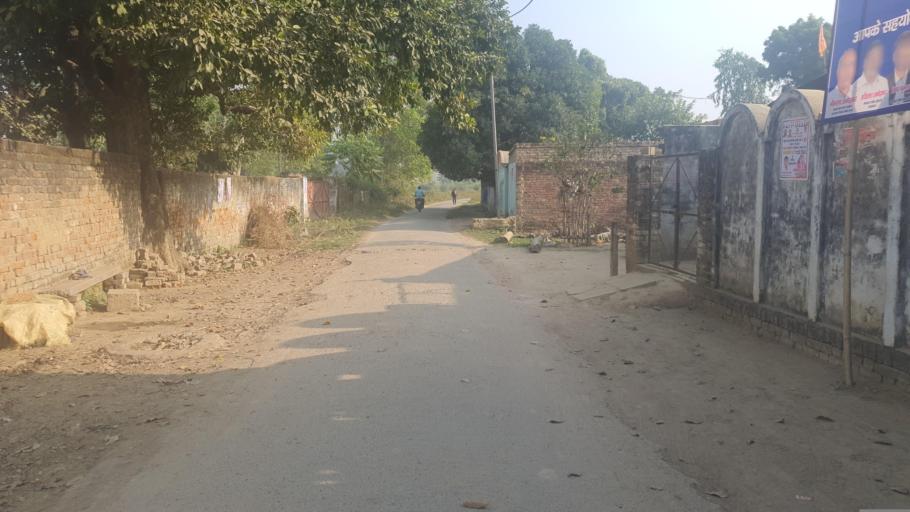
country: IN
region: Uttar Pradesh
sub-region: Lucknow District
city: Goshainganj
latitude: 26.7733
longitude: 81.0126
